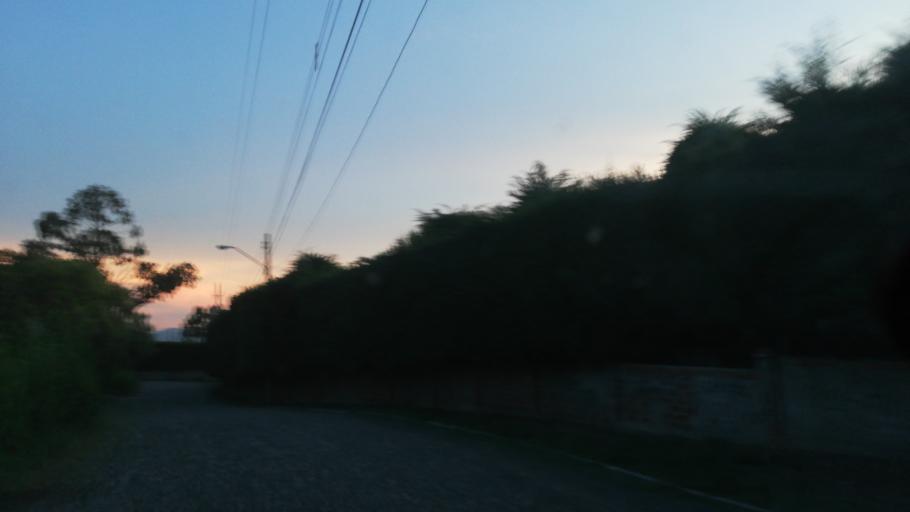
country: BO
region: Cochabamba
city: Cochabamba
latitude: -17.3241
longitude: -66.2084
